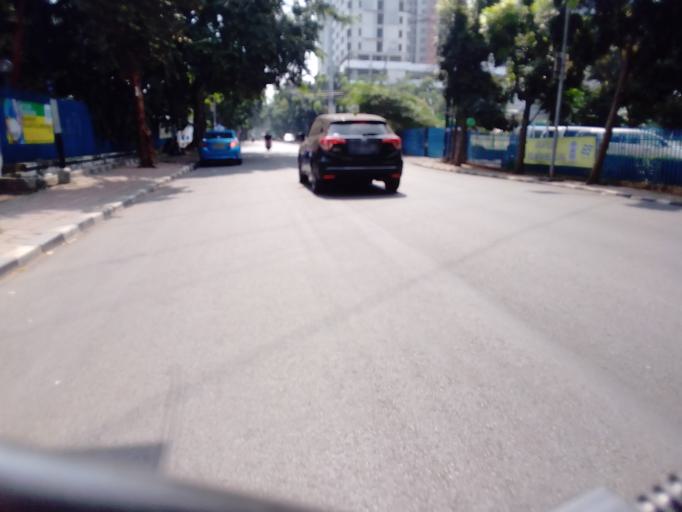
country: ID
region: Jakarta Raya
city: Jakarta
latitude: -6.2040
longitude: 106.8085
